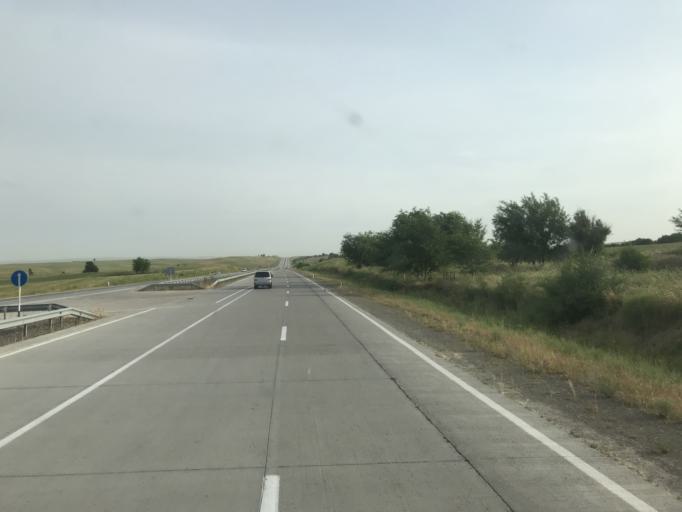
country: KZ
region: Ongtustik Qazaqstan
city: Qazyqurt
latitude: 41.6154
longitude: 69.4030
